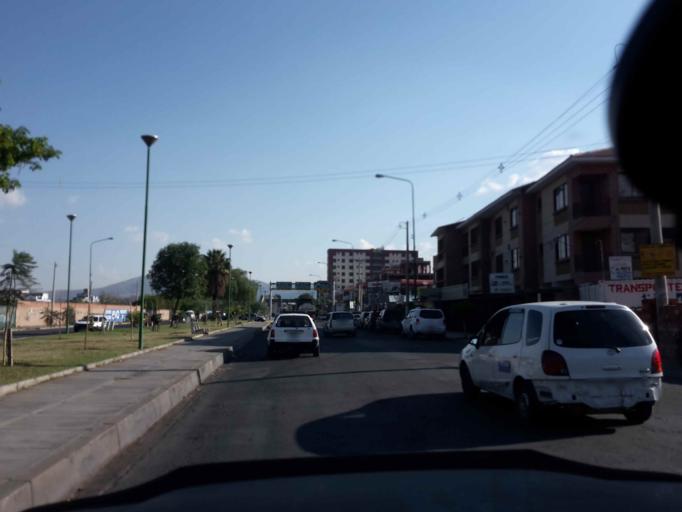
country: BO
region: Cochabamba
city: Cochabamba
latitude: -17.3887
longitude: -66.1829
